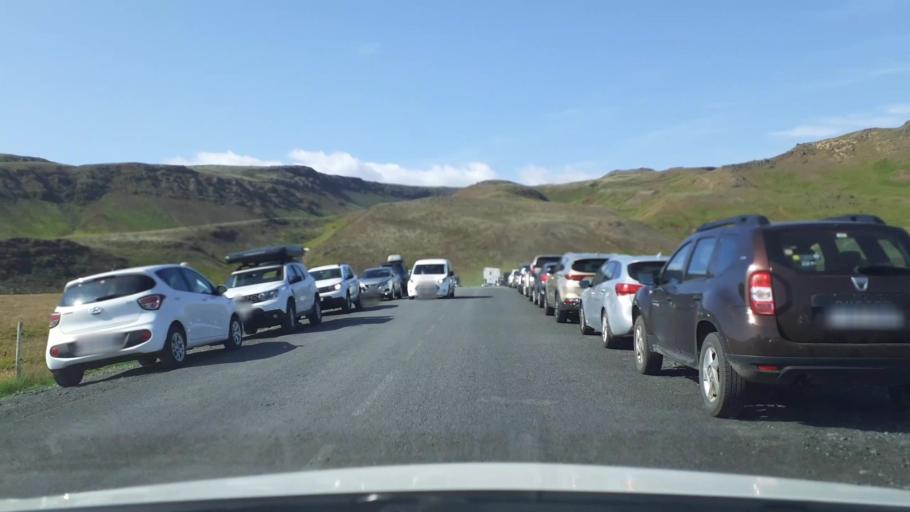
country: IS
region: South
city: Hveragerdi
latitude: 64.0208
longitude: -21.2093
